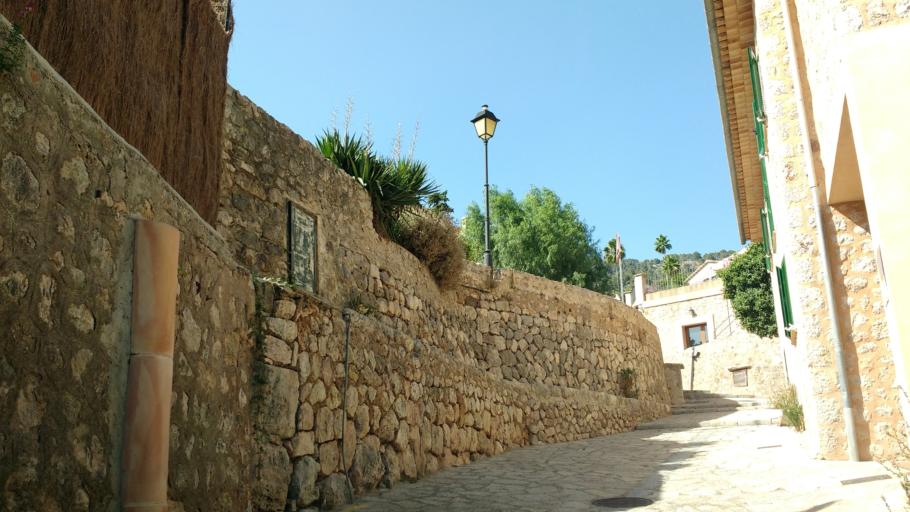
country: ES
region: Balearic Islands
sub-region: Illes Balears
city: Fornalutx
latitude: 39.7807
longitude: 2.7394
